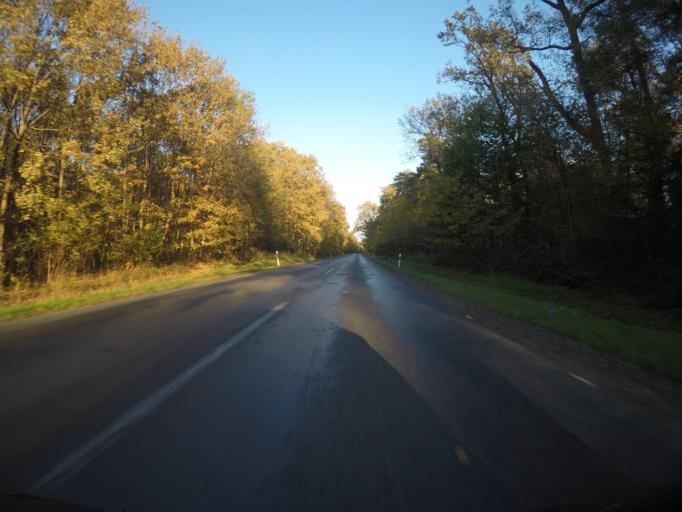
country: HU
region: Somogy
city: Barcs
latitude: 45.9737
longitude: 17.5441
